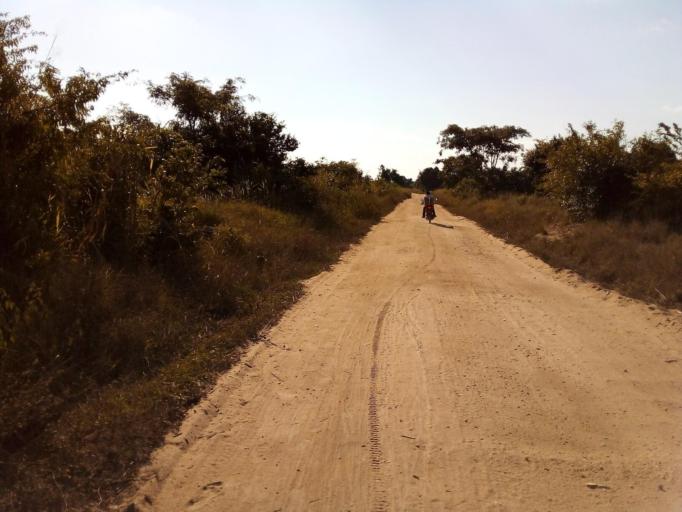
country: MZ
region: Zambezia
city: Quelimane
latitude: -17.5503
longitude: 36.6297
